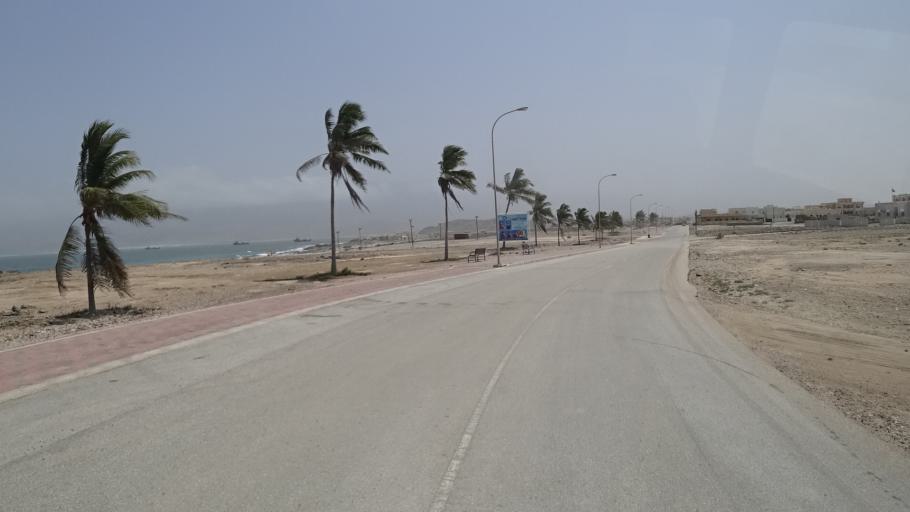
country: OM
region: Zufar
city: Salalah
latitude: 16.9797
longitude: 54.6869
